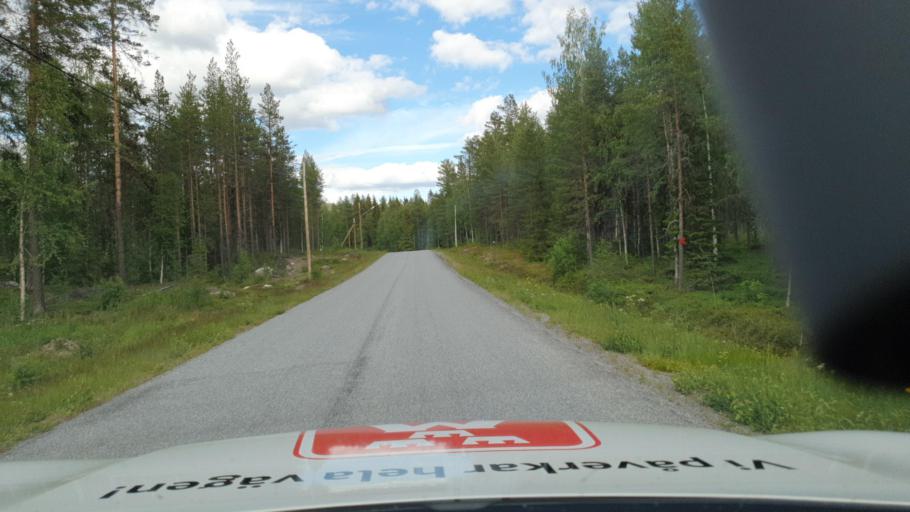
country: SE
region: Vaesterbotten
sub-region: Asele Kommun
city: Insjon
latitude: 64.1909
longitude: 17.7862
